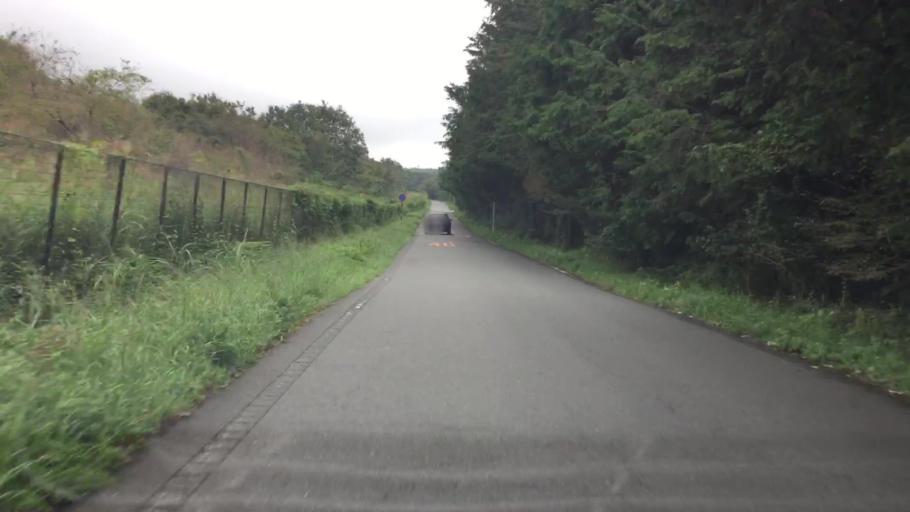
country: JP
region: Shizuoka
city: Fujinomiya
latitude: 35.3691
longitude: 138.5826
